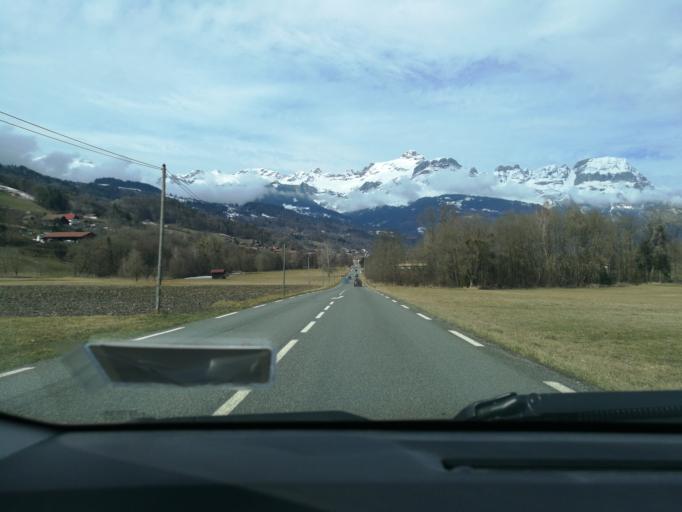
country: FR
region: Rhone-Alpes
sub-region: Departement de la Haute-Savoie
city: Passy
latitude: 45.9046
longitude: 6.6742
